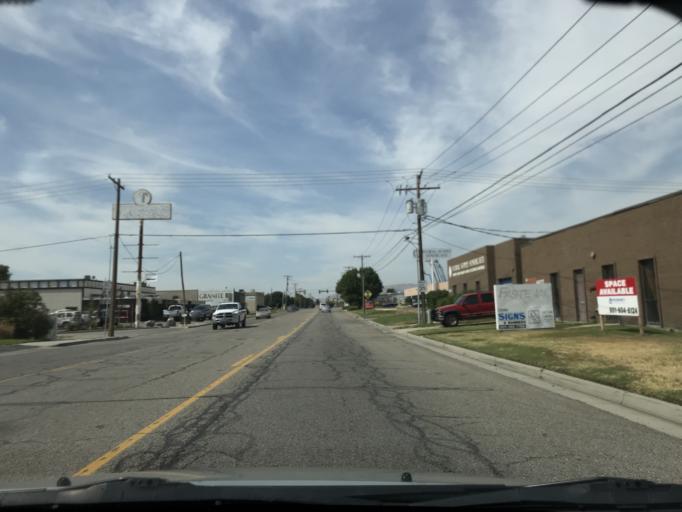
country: US
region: Utah
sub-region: Salt Lake County
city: Centerfield
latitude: 40.6756
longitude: -111.9054
